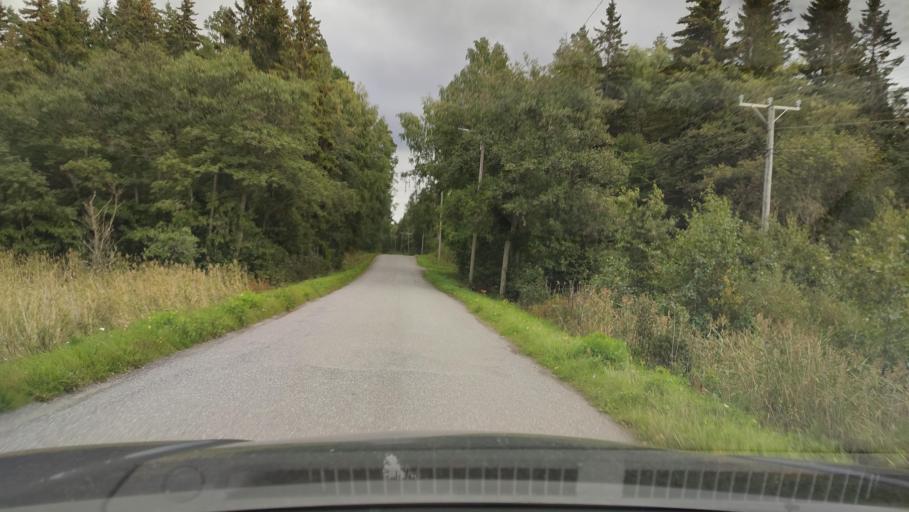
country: FI
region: Ostrobothnia
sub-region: Sydosterbotten
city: Kristinestad
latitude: 62.2496
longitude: 21.3422
